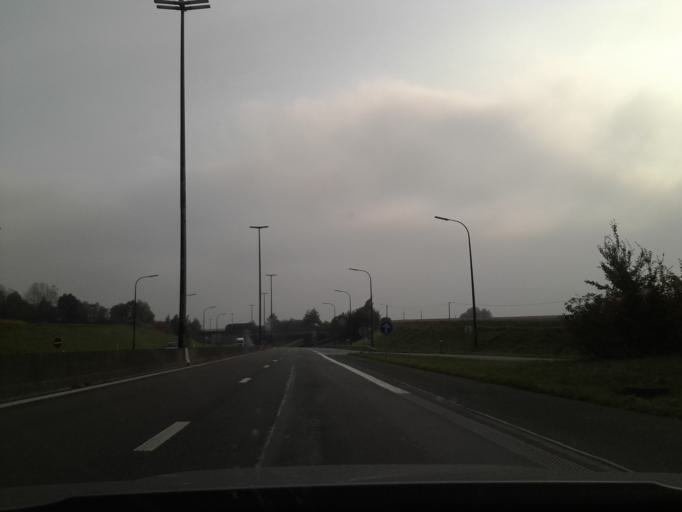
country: BE
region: Wallonia
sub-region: Province du Hainaut
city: Frasnes-lez-Buissenal
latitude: 50.6585
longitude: 3.5963
